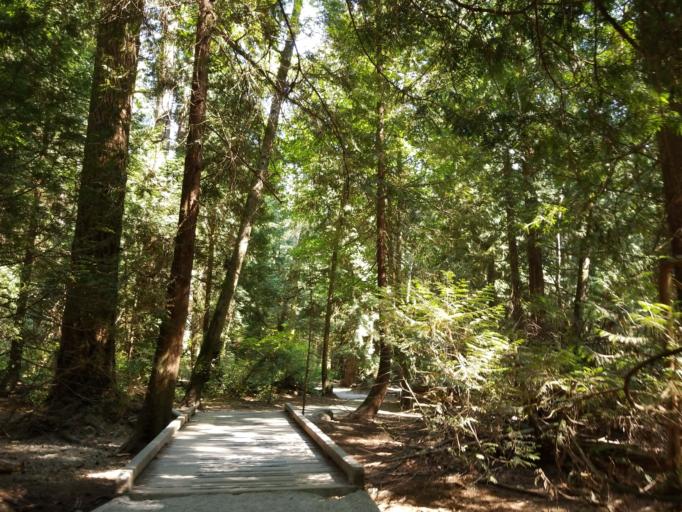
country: CA
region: British Columbia
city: West End
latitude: 49.2515
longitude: -123.2151
